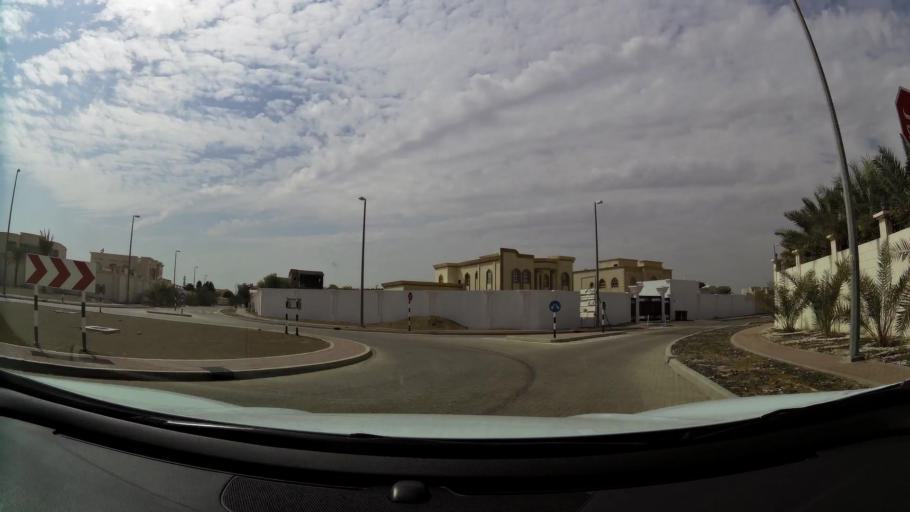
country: AE
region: Abu Dhabi
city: Al Ain
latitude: 24.1952
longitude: 55.8085
